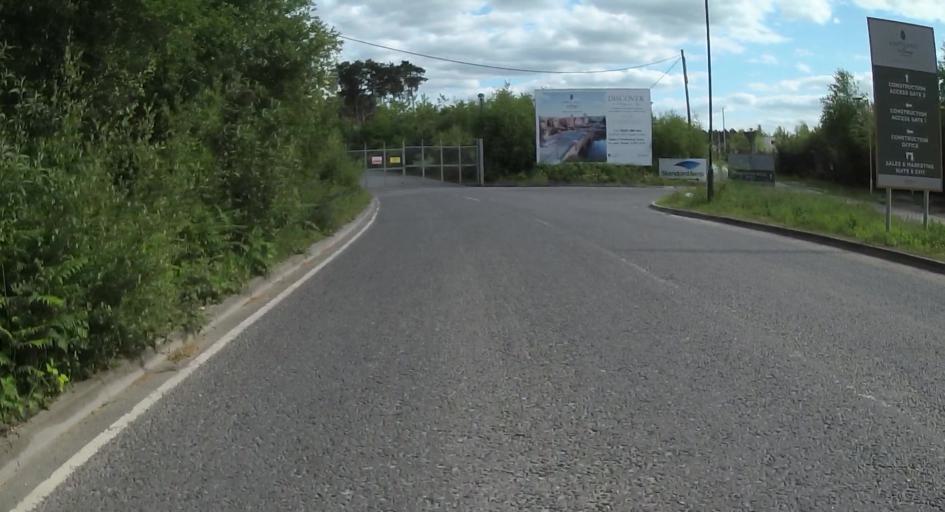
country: GB
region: England
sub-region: Hampshire
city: Fleet
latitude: 51.2857
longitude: -0.8041
